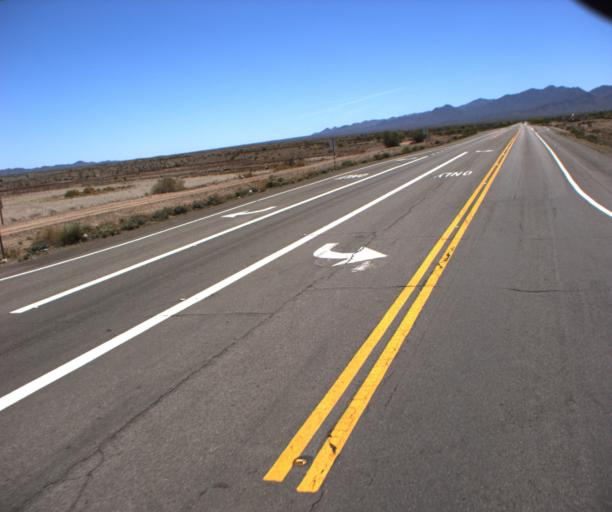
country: US
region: Arizona
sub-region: Mohave County
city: Desert Hills
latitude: 34.7228
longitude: -114.3137
